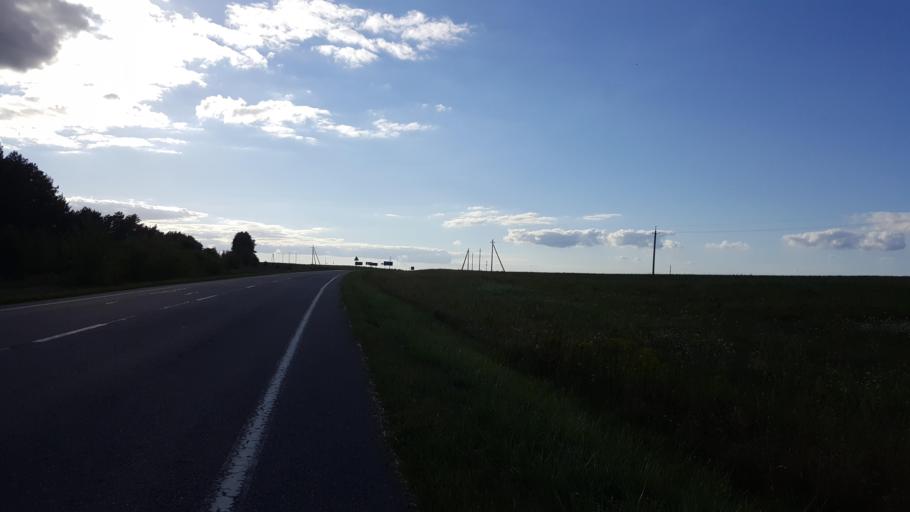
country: BY
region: Brest
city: Kamyanyets
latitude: 52.4019
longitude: 23.8709
